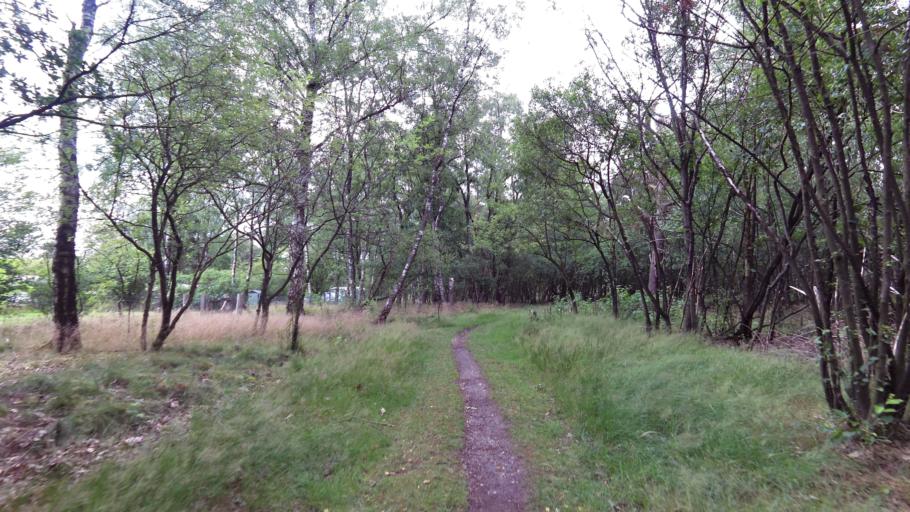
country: NL
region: Gelderland
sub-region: Gemeente Apeldoorn
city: Uddel
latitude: 52.1999
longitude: 5.8452
